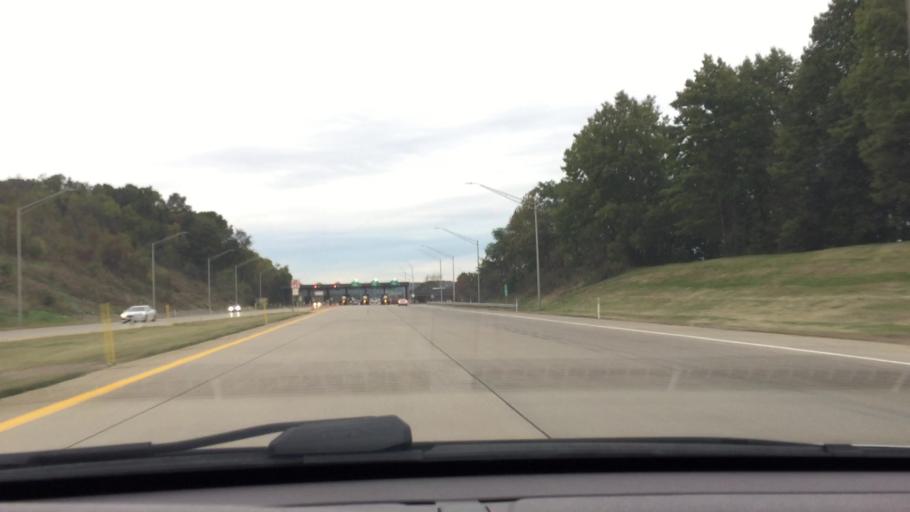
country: US
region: Pennsylvania
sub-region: Lawrence County
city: Oakland
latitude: 40.9428
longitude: -80.3914
